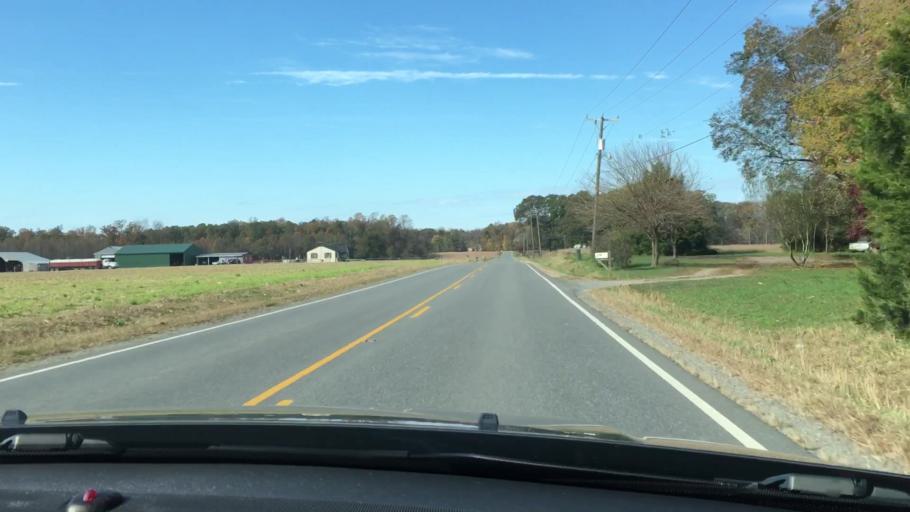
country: US
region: Virginia
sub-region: King William County
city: West Point
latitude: 37.5848
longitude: -76.8523
